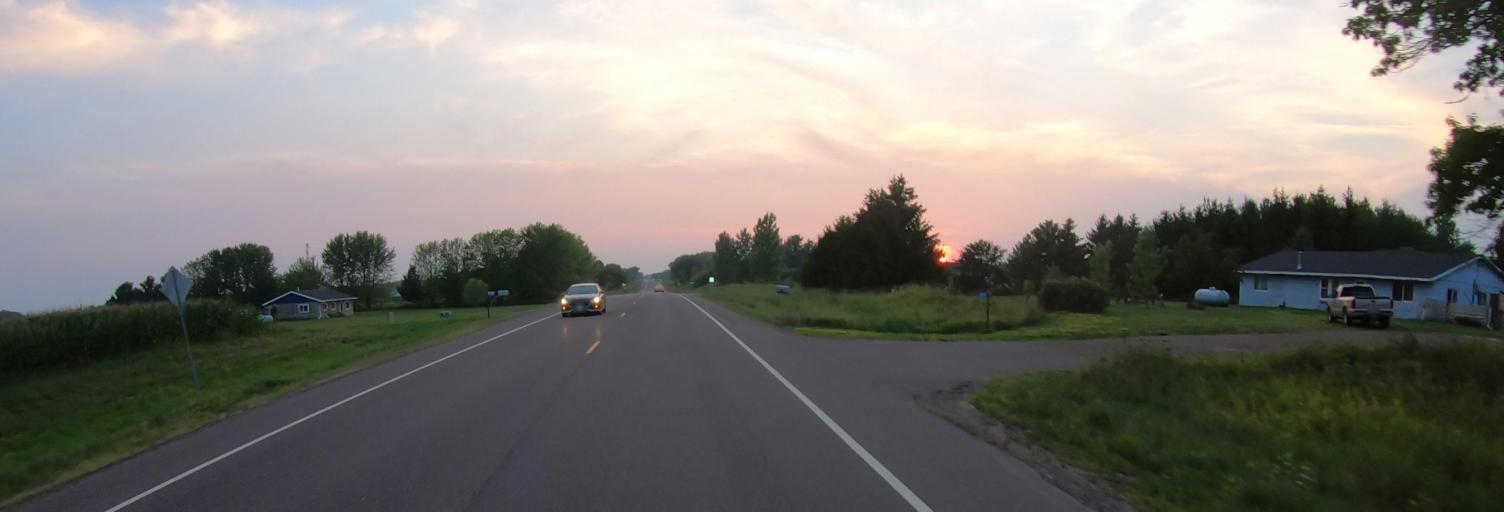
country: US
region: Minnesota
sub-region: Pine County
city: Rock Creek
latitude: 45.7736
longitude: -92.9431
